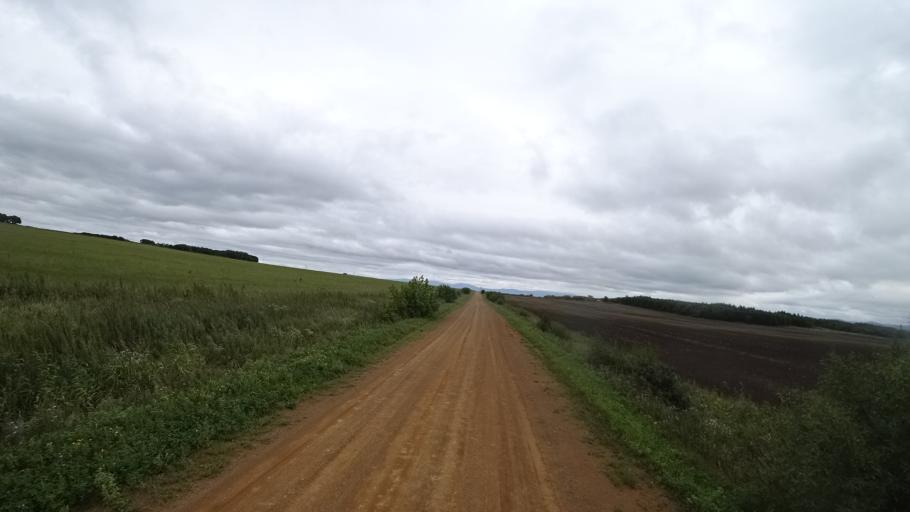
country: RU
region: Primorskiy
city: Chernigovka
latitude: 44.4362
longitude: 132.5857
